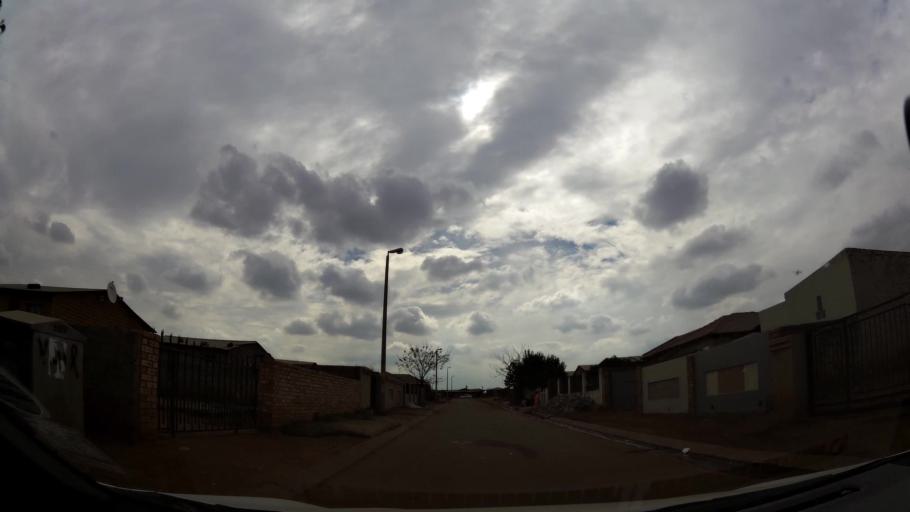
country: ZA
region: Gauteng
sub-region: Ekurhuleni Metropolitan Municipality
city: Germiston
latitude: -26.3852
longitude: 28.1217
